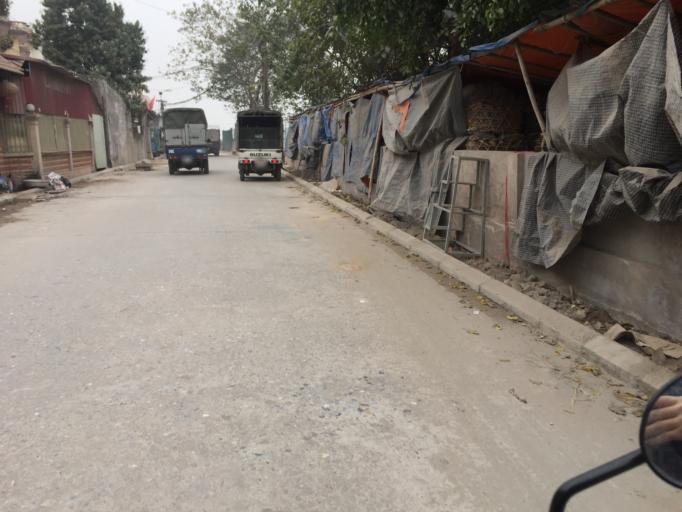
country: VN
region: Hung Yen
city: Van Giang
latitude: 20.9712
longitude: 105.9185
